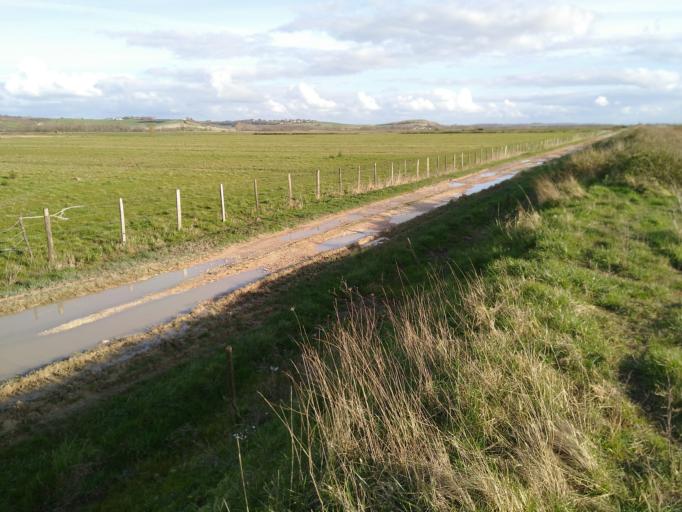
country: FR
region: Poitou-Charentes
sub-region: Departement de la Charente-Maritime
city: Mortagne-sur-Gironde
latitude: 45.4632
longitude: -0.7858
